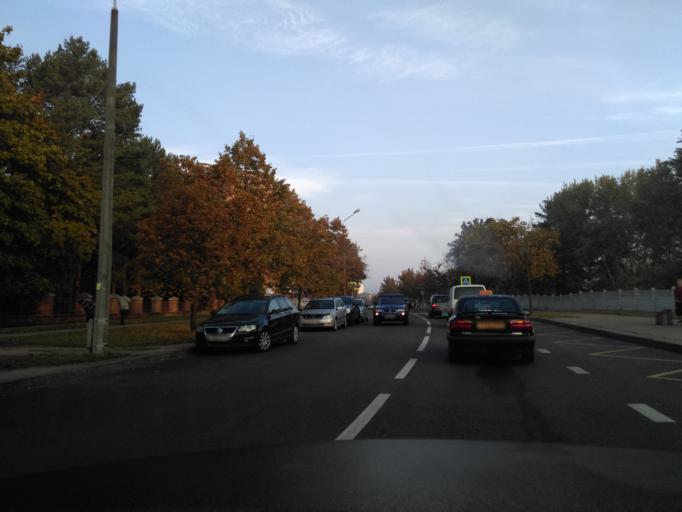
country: BY
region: Minsk
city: Minsk
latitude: 53.8612
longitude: 27.6346
